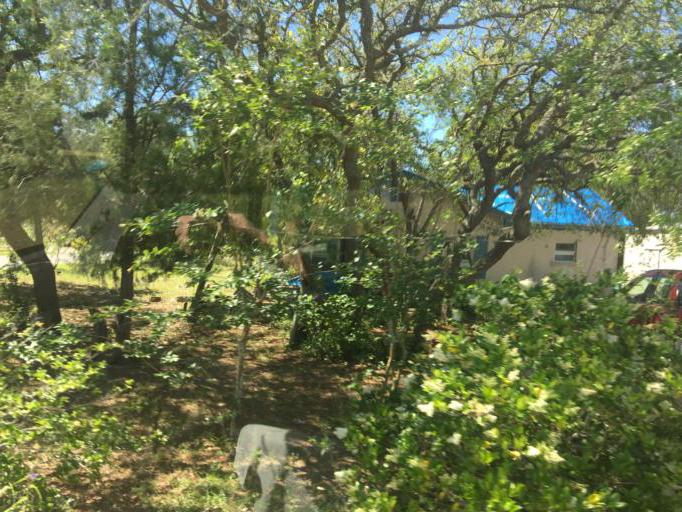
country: US
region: Florida
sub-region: Bay County
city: Panama City Beach
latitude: 30.2004
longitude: -85.8425
